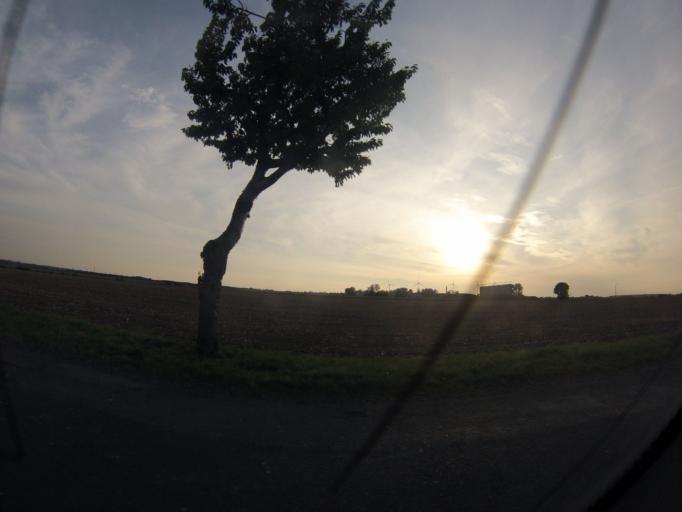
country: DE
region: Thuringia
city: Altkirchen
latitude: 50.9152
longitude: 12.3471
